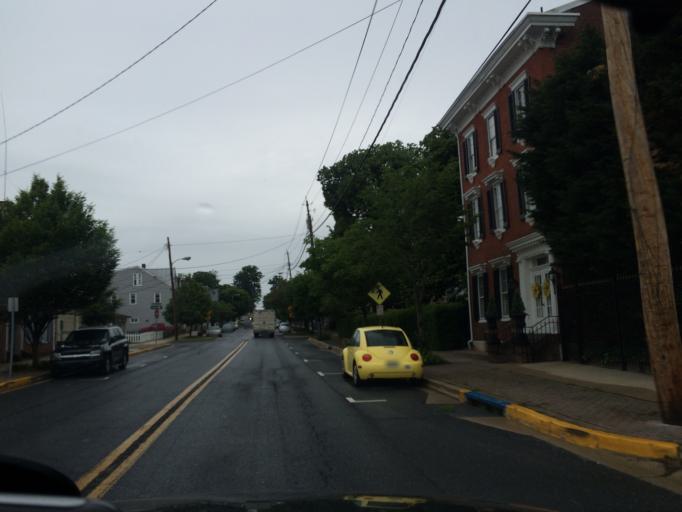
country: US
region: Maryland
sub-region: Carroll County
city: Westminster
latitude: 39.5788
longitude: -76.9996
